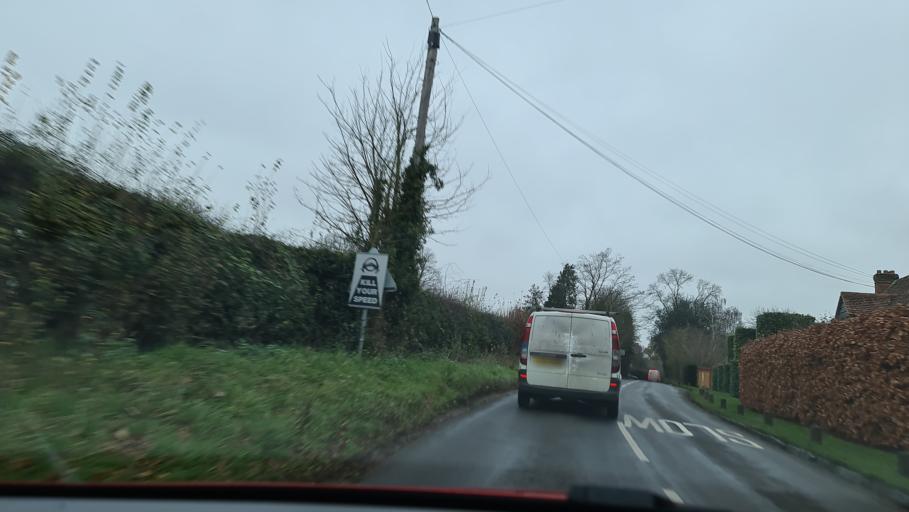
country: GB
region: England
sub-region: Buckinghamshire
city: Seer Green
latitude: 51.6115
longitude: -0.5944
